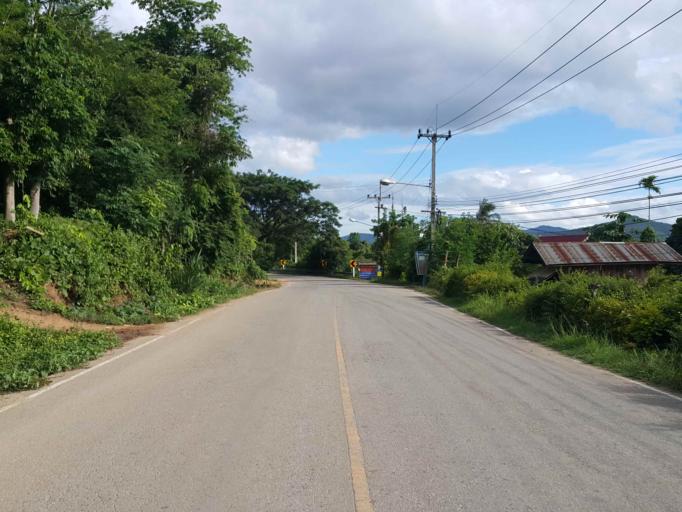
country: TH
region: Chiang Mai
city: Mae Chaem
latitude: 18.4814
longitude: 98.3764
